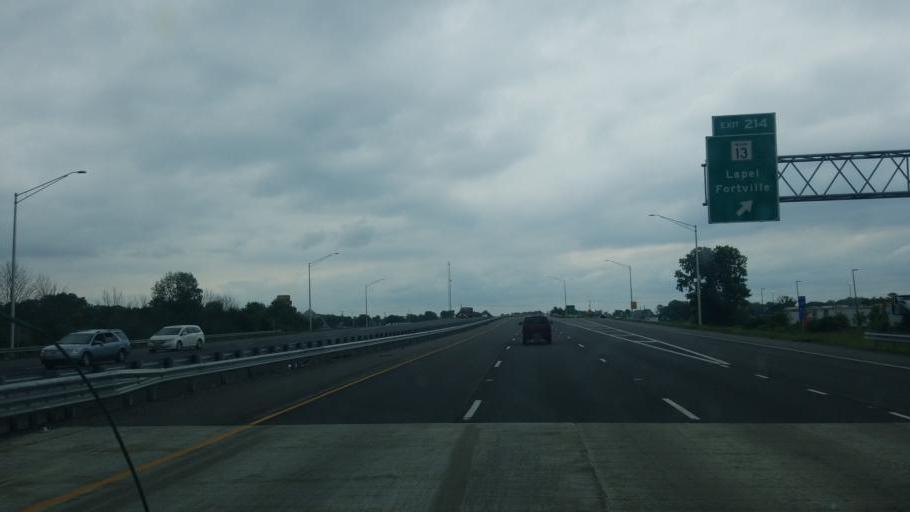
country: US
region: Indiana
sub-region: Madison County
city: Ingalls
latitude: 39.9934
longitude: -85.8484
